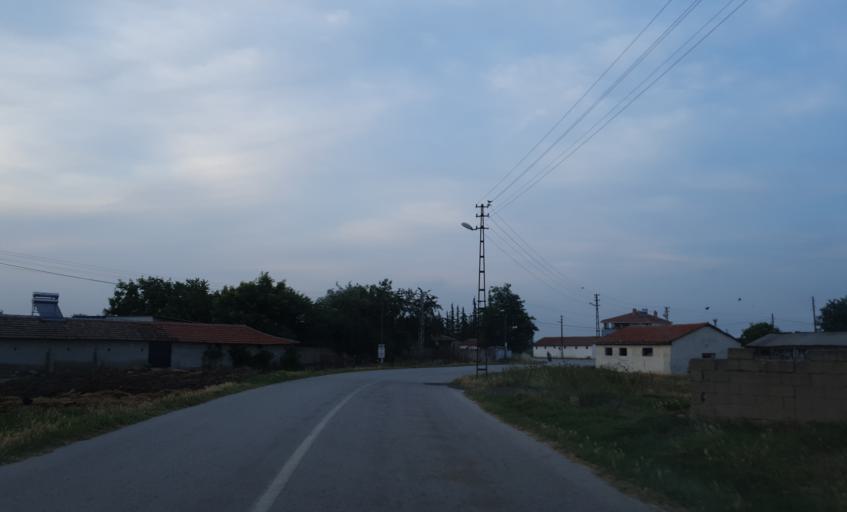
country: TR
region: Kirklareli
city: Buyukkaristiran
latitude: 41.3480
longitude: 27.6098
